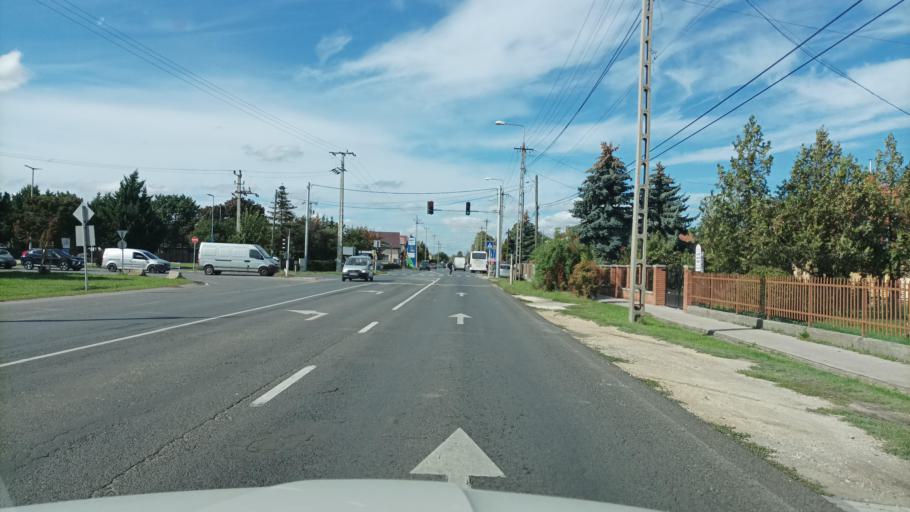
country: HU
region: Pest
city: Ullo
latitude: 47.3804
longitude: 19.3550
